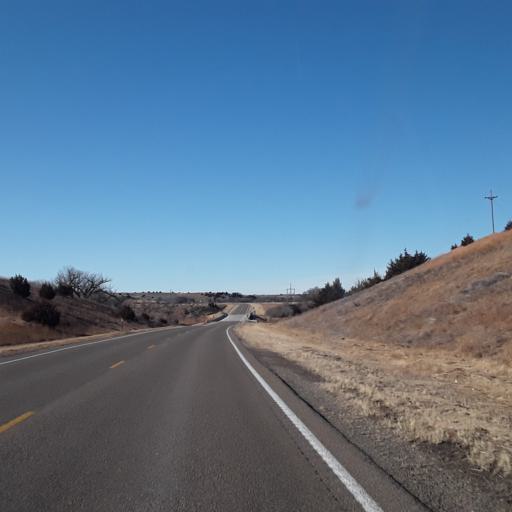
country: US
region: Nebraska
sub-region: Frontier County
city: Stockville
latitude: 40.6312
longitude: -100.5634
